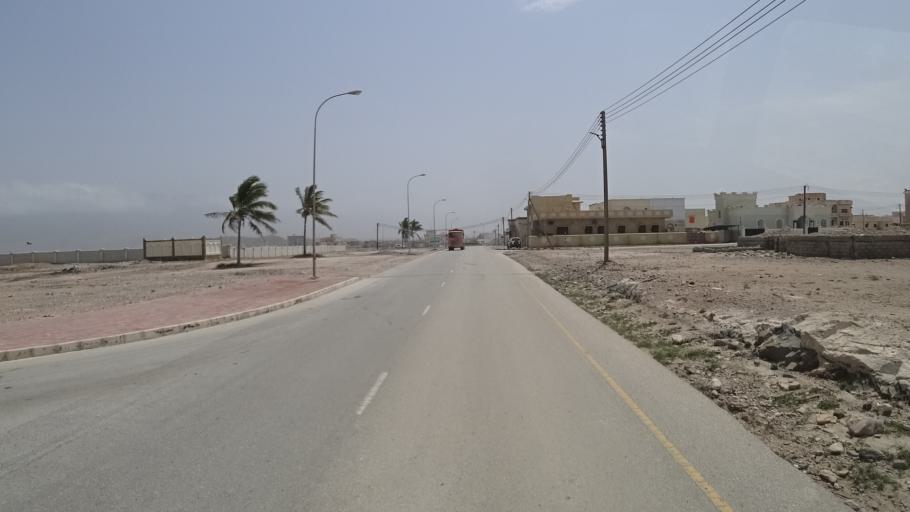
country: OM
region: Zufar
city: Salalah
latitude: 16.9815
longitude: 54.6878
